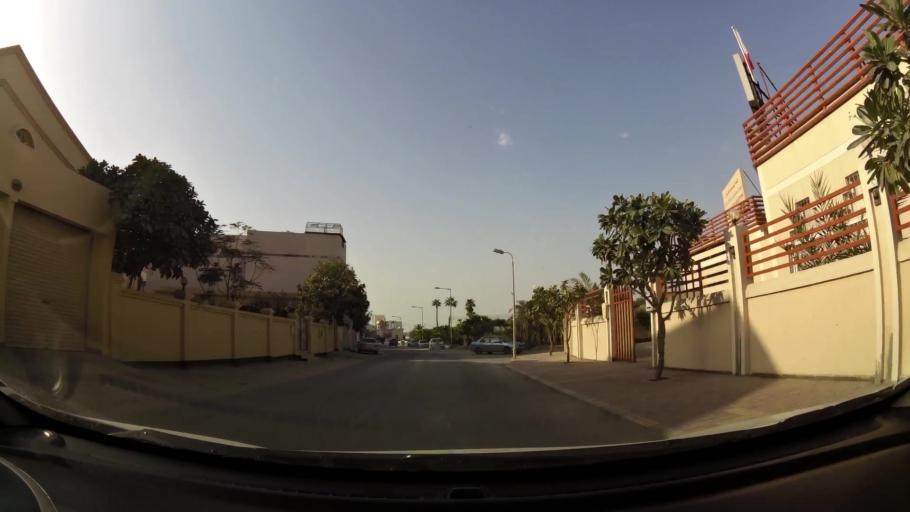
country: BH
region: Manama
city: Jidd Hafs
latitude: 26.2145
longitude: 50.5038
